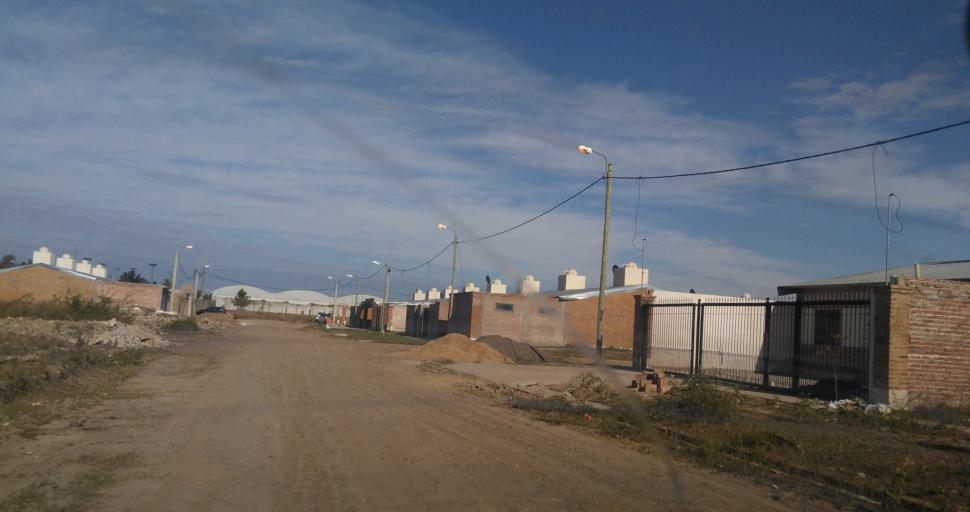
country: AR
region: Chaco
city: Fontana
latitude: -27.4045
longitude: -58.9796
